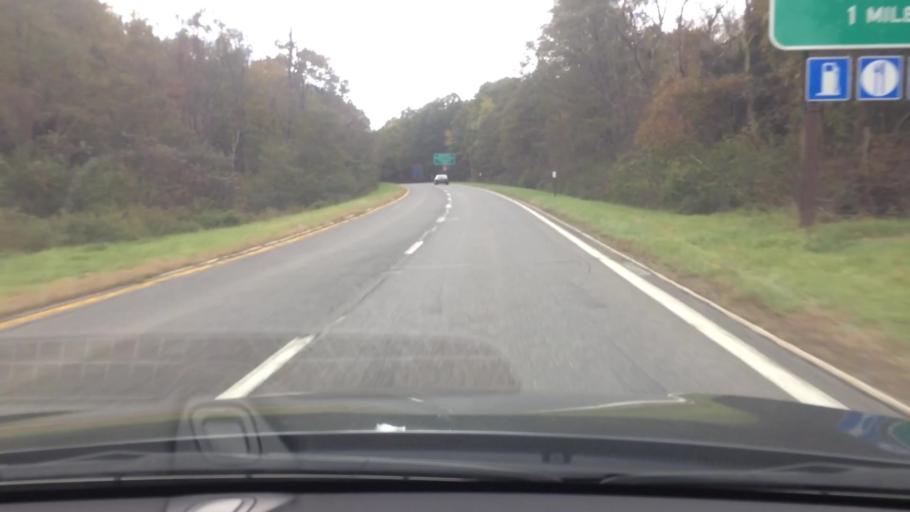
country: US
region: New York
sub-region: Dutchess County
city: Pine Plains
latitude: 41.9724
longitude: -73.7520
